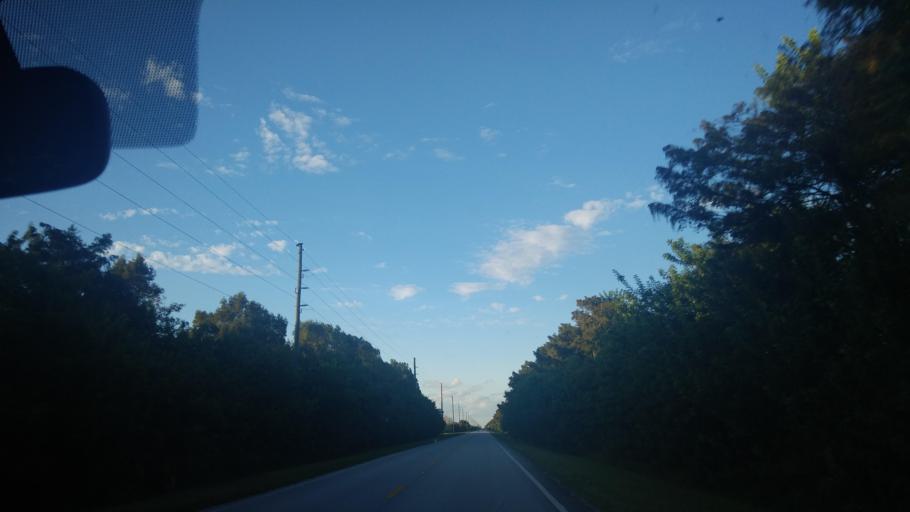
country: US
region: Florida
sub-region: Indian River County
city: Fellsmere
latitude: 27.6604
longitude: -80.6433
